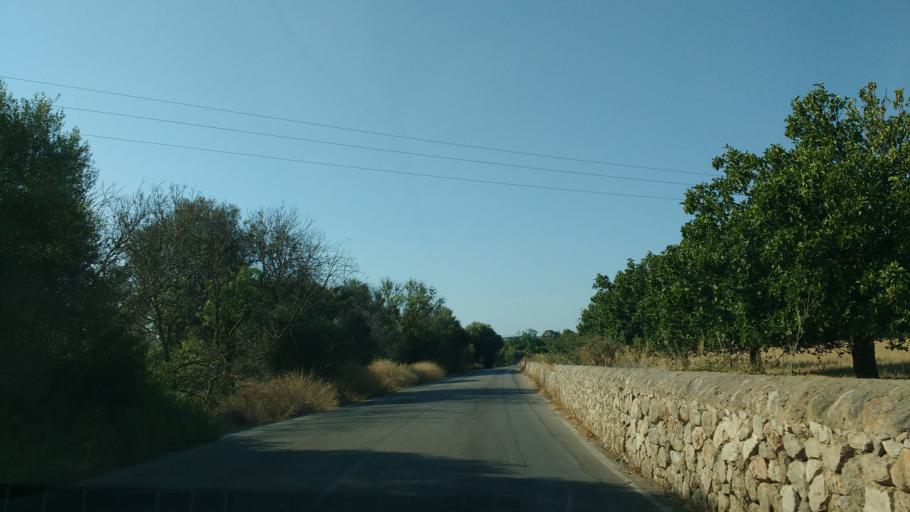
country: ES
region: Balearic Islands
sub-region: Illes Balears
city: Consell
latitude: 39.6830
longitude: 2.8121
